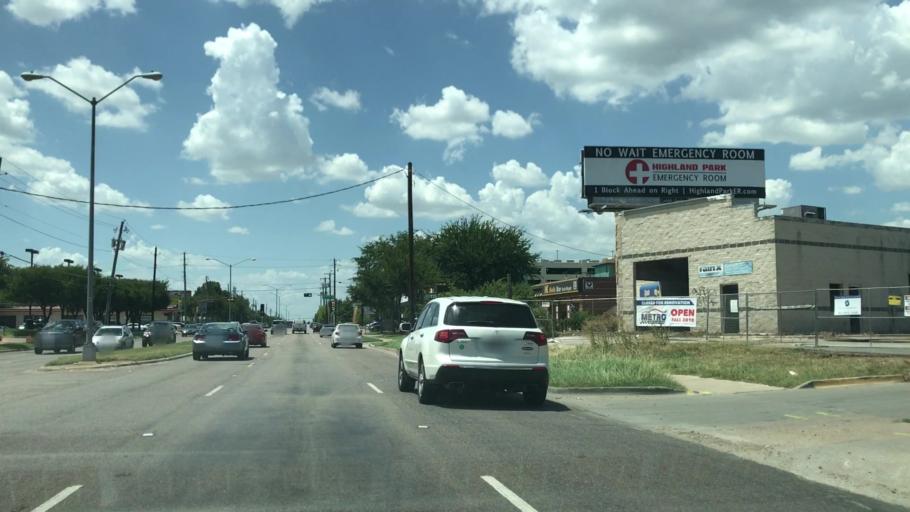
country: US
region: Texas
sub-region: Dallas County
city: Highland Park
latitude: 32.8232
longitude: -96.8186
